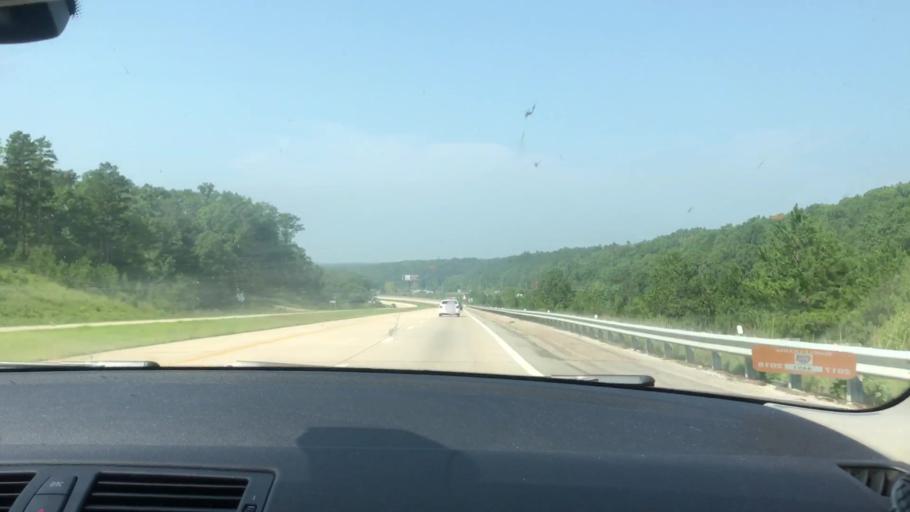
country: US
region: Missouri
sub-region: Carter County
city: Van Buren
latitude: 37.0153
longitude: -90.9852
